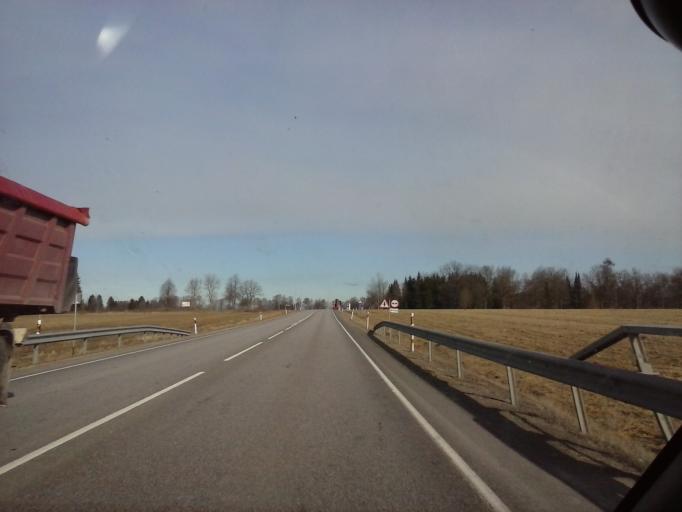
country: EE
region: Jaervamaa
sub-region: Paide linn
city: Paide
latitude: 58.8284
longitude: 25.7456
